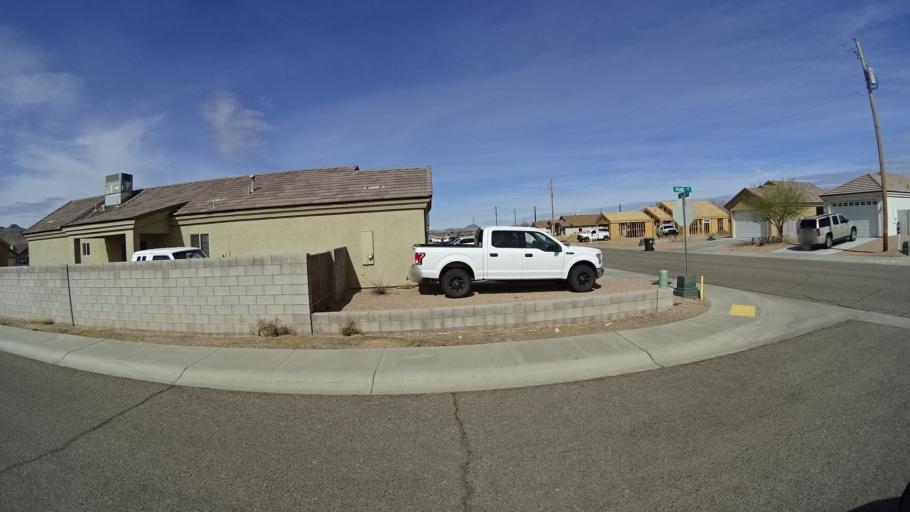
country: US
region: Arizona
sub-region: Mohave County
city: New Kingman-Butler
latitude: 35.2302
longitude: -114.0210
